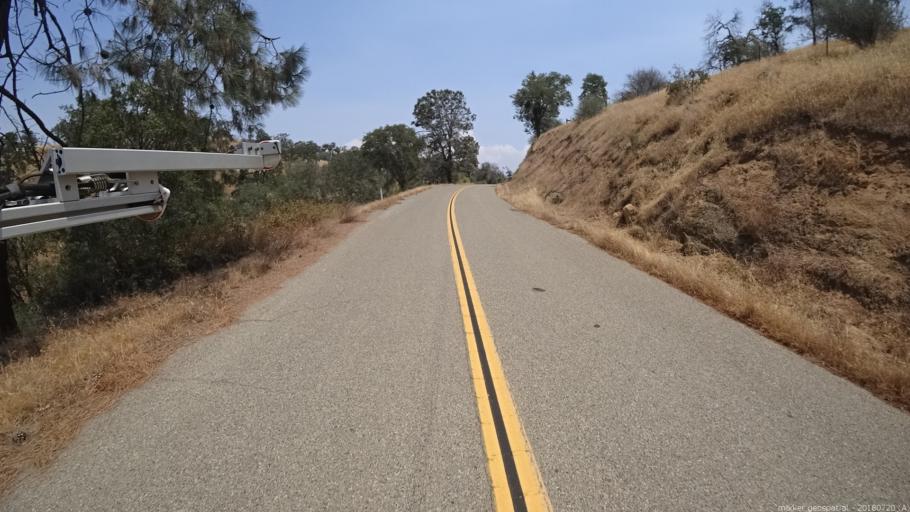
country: US
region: California
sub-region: Madera County
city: Yosemite Lakes
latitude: 37.2753
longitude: -119.8371
